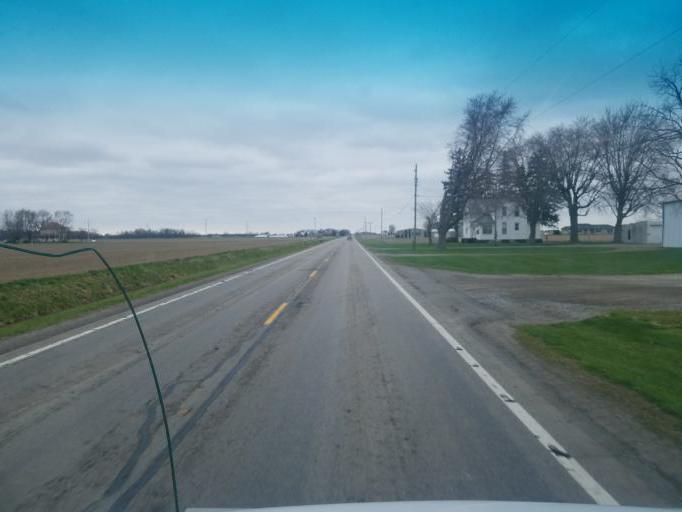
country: US
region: Ohio
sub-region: Allen County
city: Delphos
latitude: 40.8865
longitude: -84.3504
